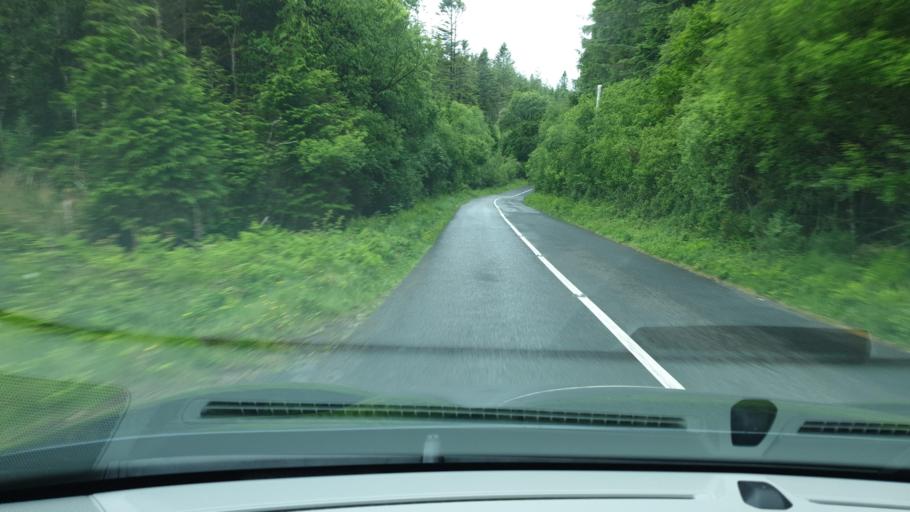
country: IE
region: Connaught
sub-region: County Galway
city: Clifden
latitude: 53.4563
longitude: -9.8469
